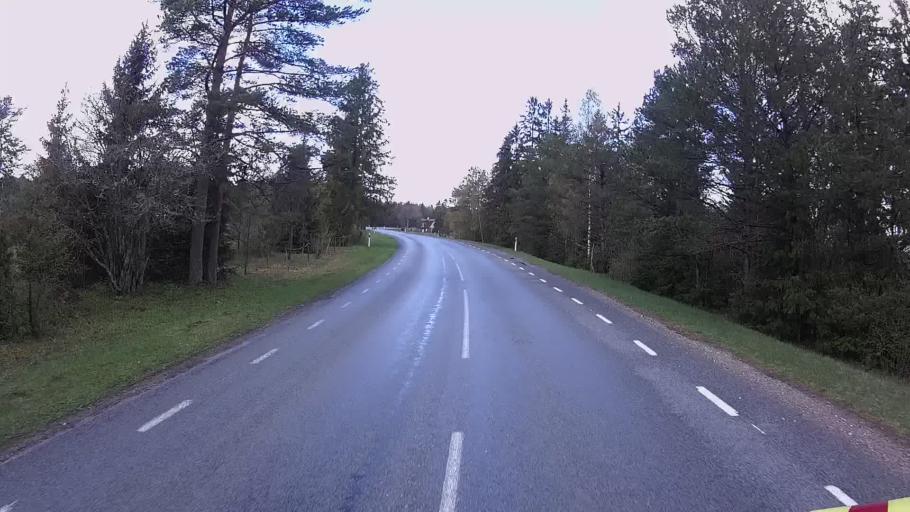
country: EE
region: Hiiumaa
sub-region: Kaerdla linn
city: Kardla
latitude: 58.9365
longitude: 22.7812
